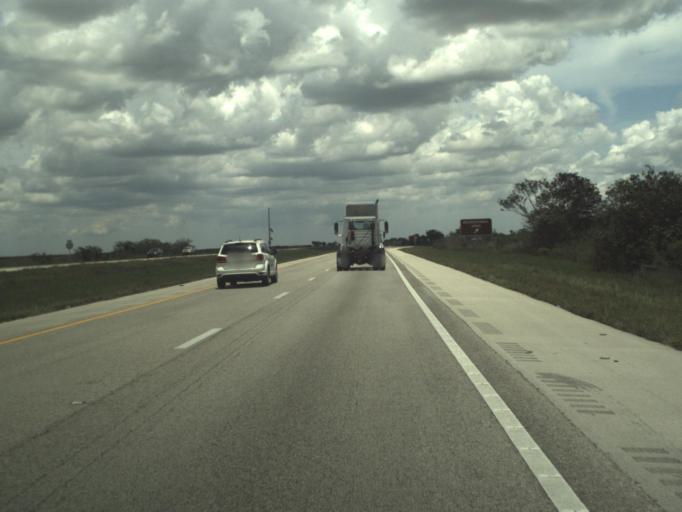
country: US
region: Florida
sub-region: Broward County
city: Weston
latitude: 26.1462
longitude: -80.5868
